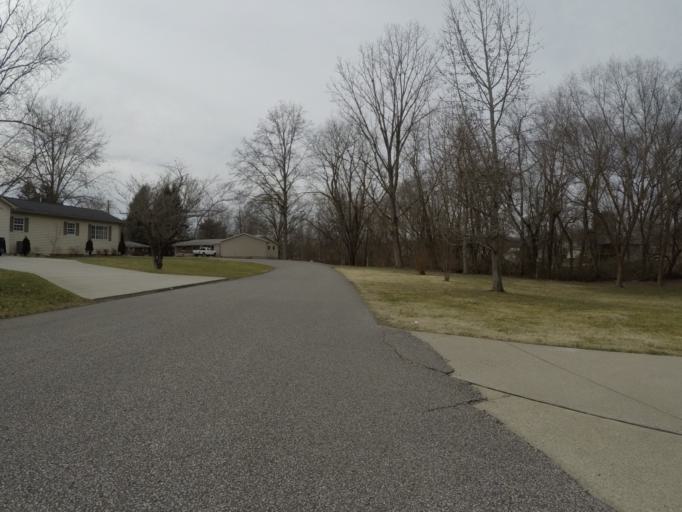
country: US
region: West Virginia
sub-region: Cabell County
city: Pea Ridge
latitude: 38.4483
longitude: -82.3451
